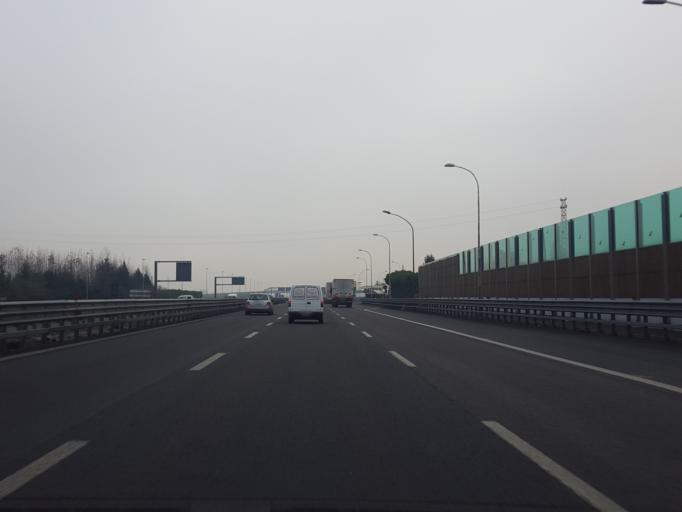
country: IT
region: Veneto
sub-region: Provincia di Vicenza
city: Torri di Quartesolo
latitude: 45.5058
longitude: 11.6206
